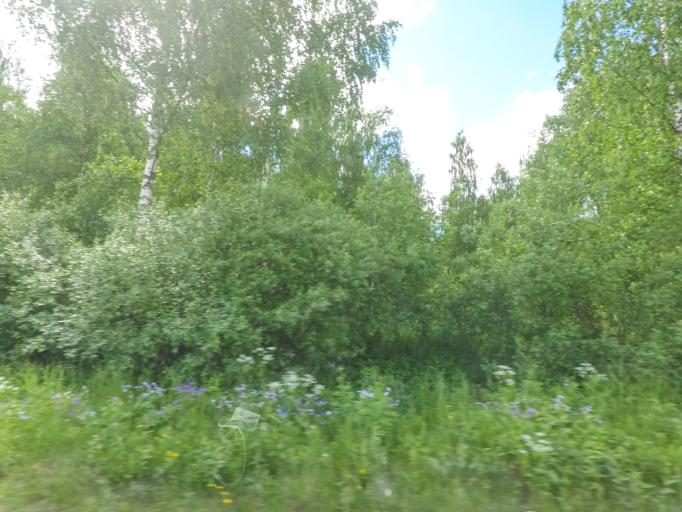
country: FI
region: Central Finland
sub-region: Jyvaeskylae
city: Hankasalmi
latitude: 62.4153
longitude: 26.6410
